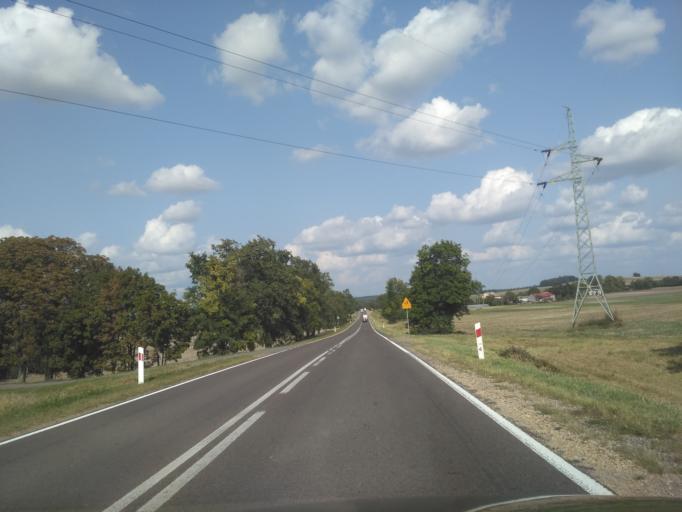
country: PL
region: Lublin Voivodeship
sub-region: Powiat chelmski
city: Rejowiec
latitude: 51.1089
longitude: 23.3146
